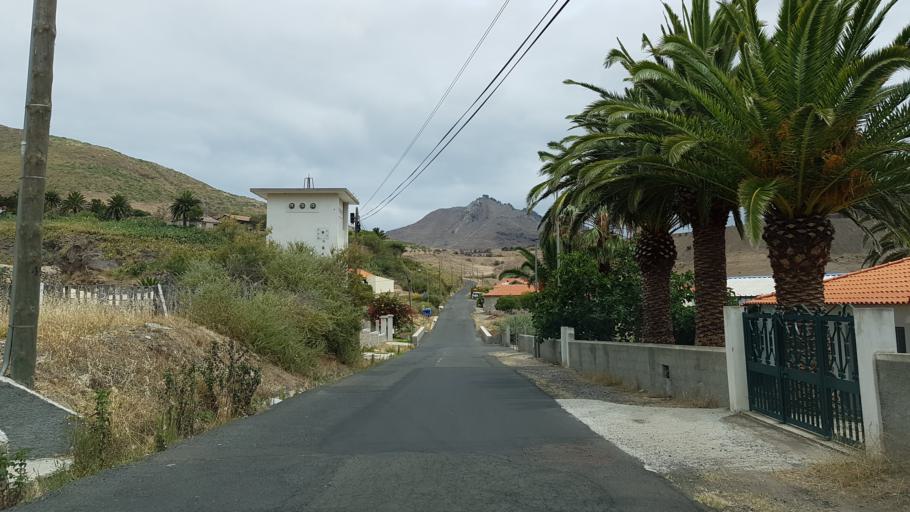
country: PT
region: Madeira
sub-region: Porto Santo
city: Vila de Porto Santo
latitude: 33.0727
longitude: -16.3134
